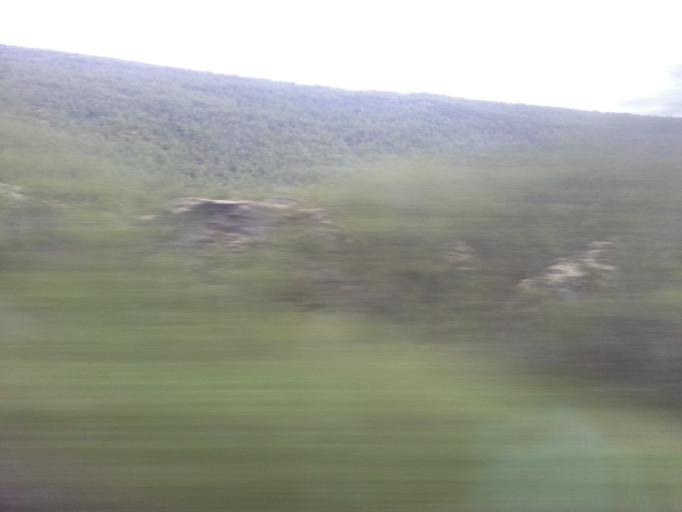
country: NO
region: Sor-Trondelag
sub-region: Oppdal
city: Oppdal
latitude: 62.3124
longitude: 9.6108
